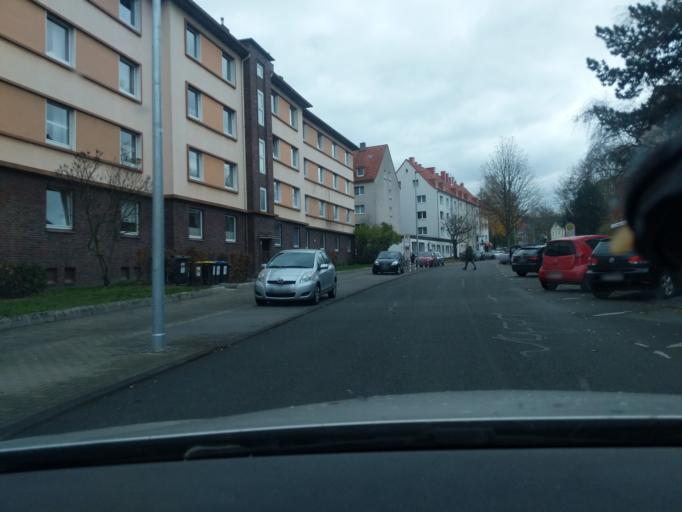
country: DE
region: North Rhine-Westphalia
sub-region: Regierungsbezirk Arnsberg
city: Dortmund
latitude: 51.5056
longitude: 7.4452
